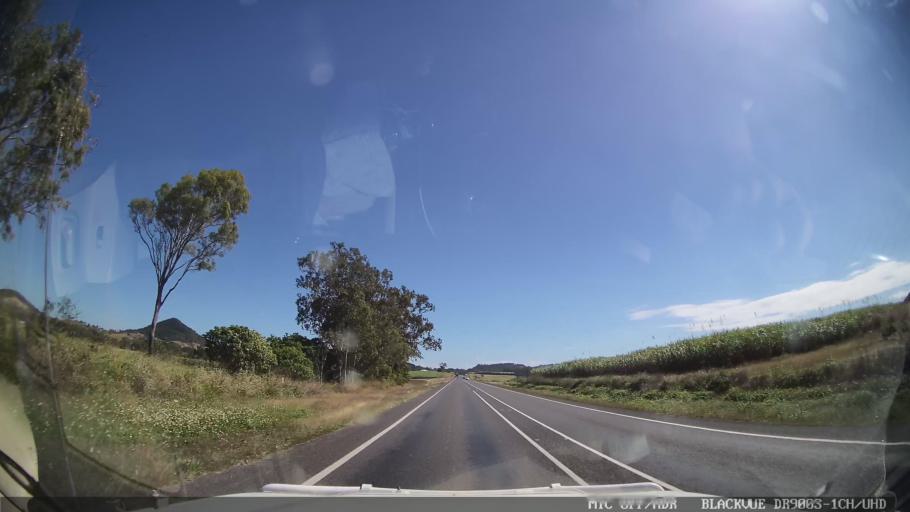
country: AU
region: Queensland
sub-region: Mackay
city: Walkerston
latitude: -21.0906
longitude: 149.0520
